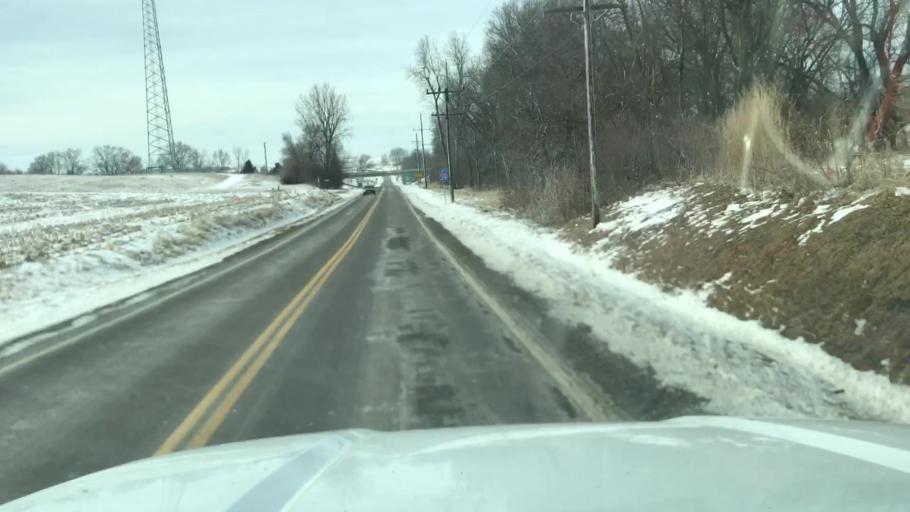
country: US
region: Missouri
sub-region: Holt County
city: Oregon
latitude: 40.0478
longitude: -95.1365
